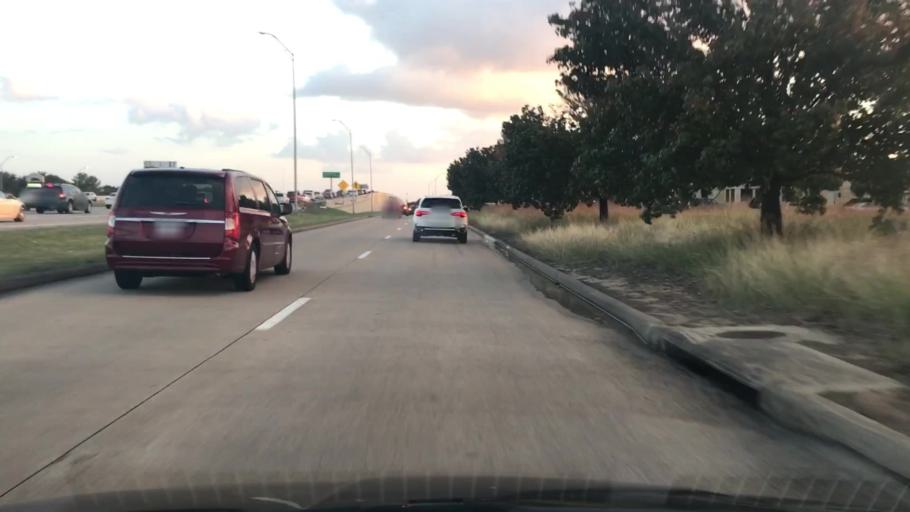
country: US
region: Texas
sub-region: Fort Bend County
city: Cinco Ranch
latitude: 29.7603
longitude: -95.7767
